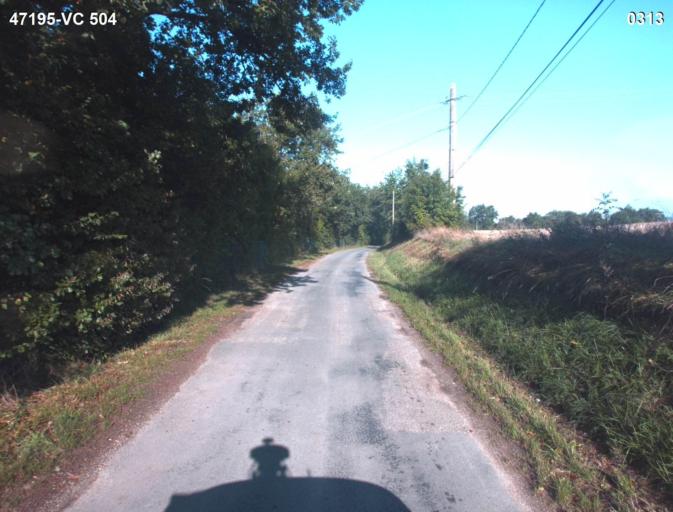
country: FR
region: Aquitaine
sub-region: Departement du Lot-et-Garonne
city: Nerac
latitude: 44.1506
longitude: 0.3355
